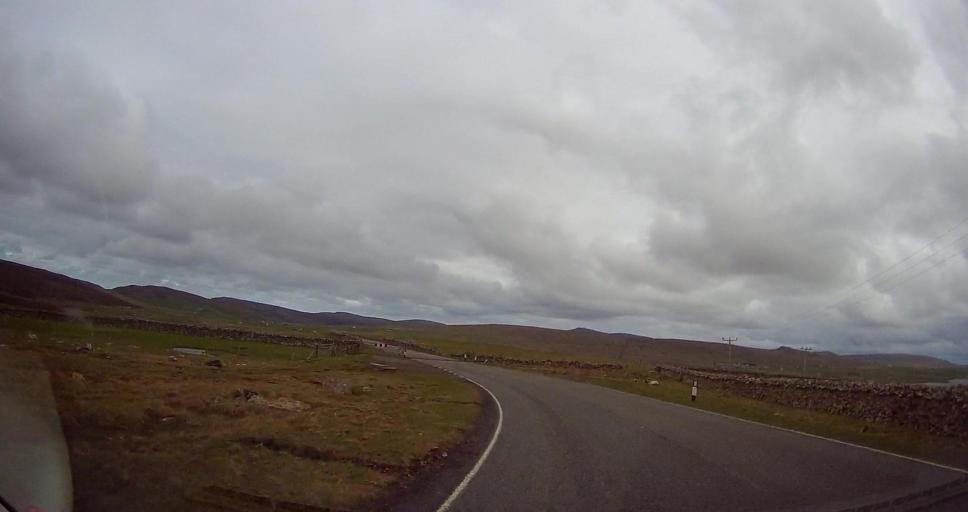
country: GB
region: Scotland
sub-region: Shetland Islands
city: Shetland
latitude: 60.7438
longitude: -0.8844
